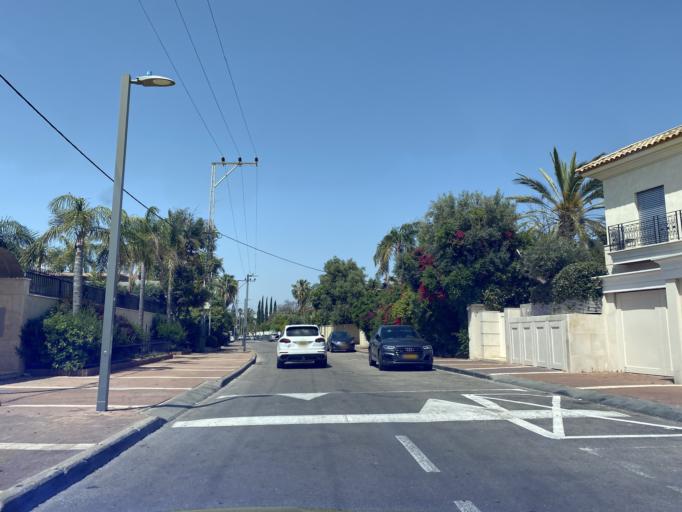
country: IL
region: Tel Aviv
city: Herzliya Pituah
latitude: 32.1749
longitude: 34.8137
